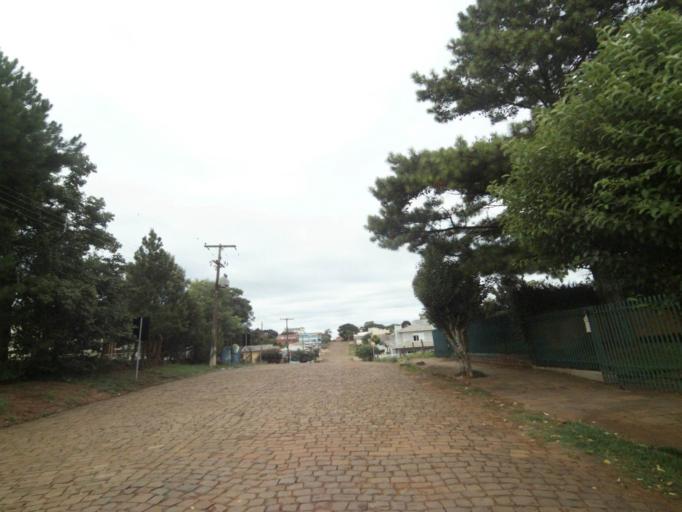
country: BR
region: Rio Grande do Sul
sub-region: Lagoa Vermelha
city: Lagoa Vermelha
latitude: -28.2160
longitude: -51.5147
